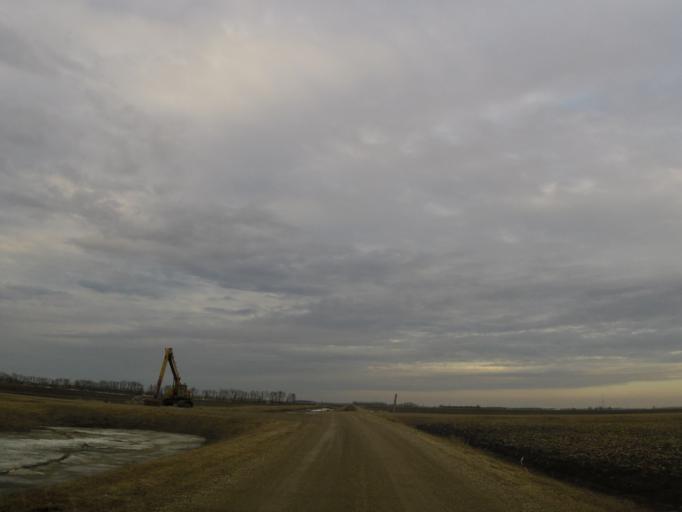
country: US
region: North Dakota
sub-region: Walsh County
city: Grafton
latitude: 48.3686
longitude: -97.2124
